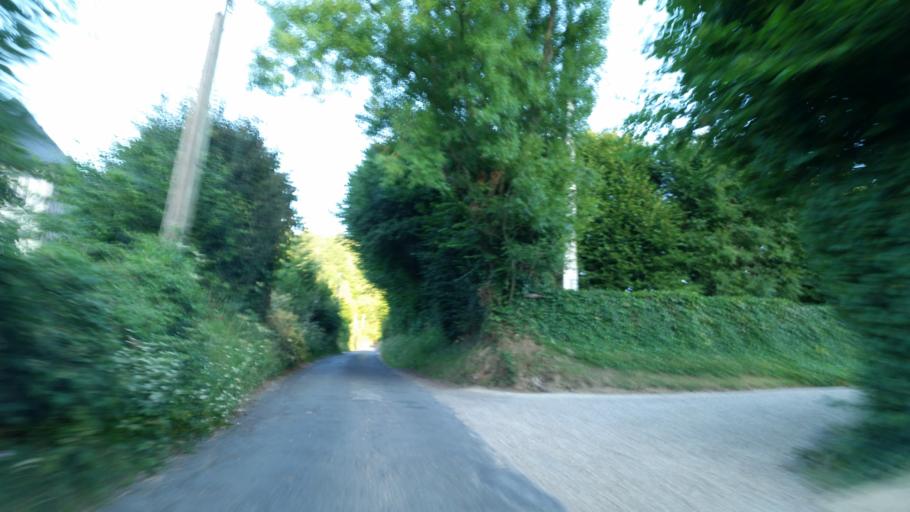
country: FR
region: Lower Normandy
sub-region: Departement du Calvados
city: Equemauville
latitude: 49.3987
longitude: 0.2221
